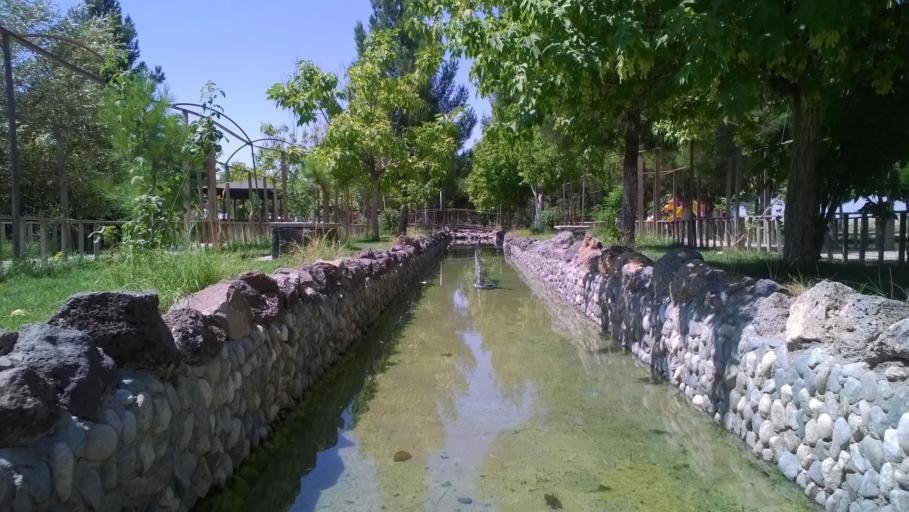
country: TR
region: Batman
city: Besiri
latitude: 37.9091
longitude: 41.2570
